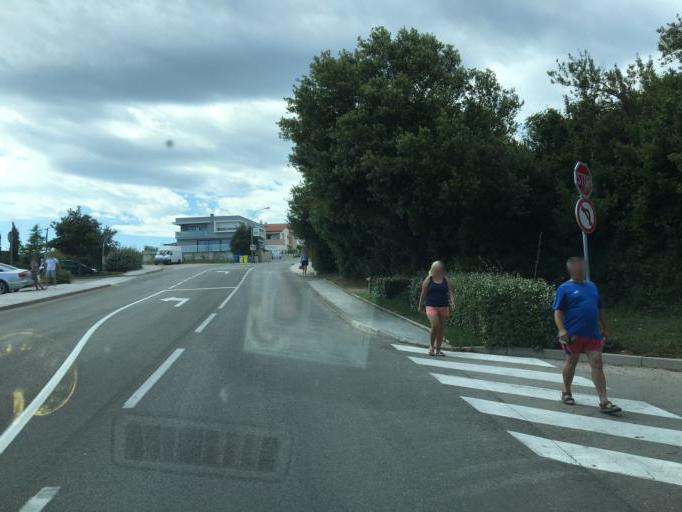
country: HR
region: Primorsko-Goranska
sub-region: Grad Krk
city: Krk
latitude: 45.0243
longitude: 14.5684
